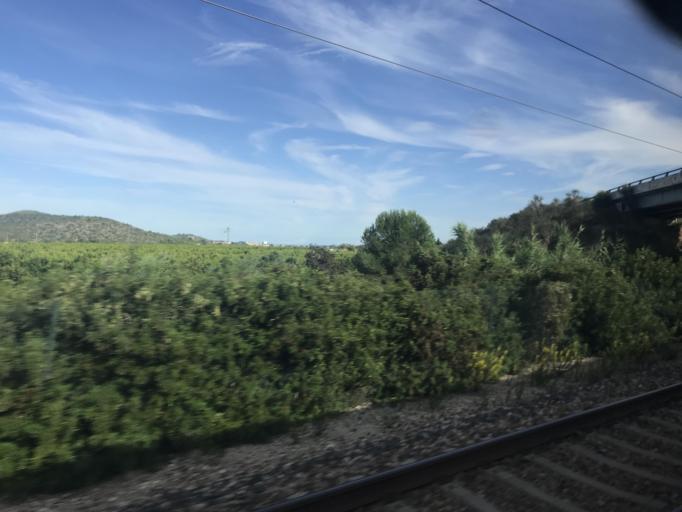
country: ES
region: Catalonia
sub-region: Provincia de Tarragona
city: Alcanar
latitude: 40.5474
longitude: 0.4301
